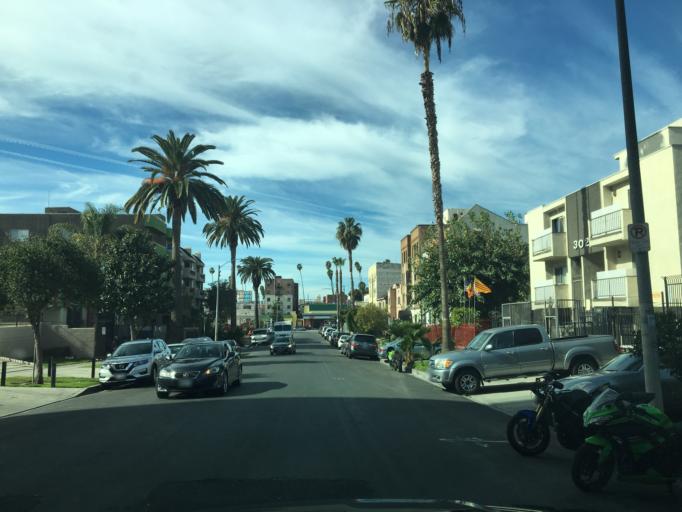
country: US
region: California
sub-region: Los Angeles County
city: Silver Lake
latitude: 34.0587
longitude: -118.2896
